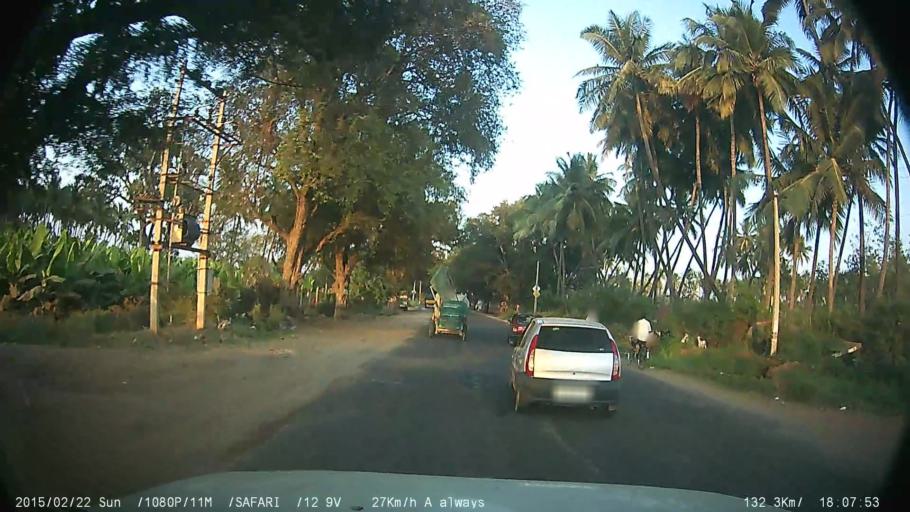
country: IN
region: Tamil Nadu
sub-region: Theni
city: Chinnamanur
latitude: 9.8349
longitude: 77.3771
